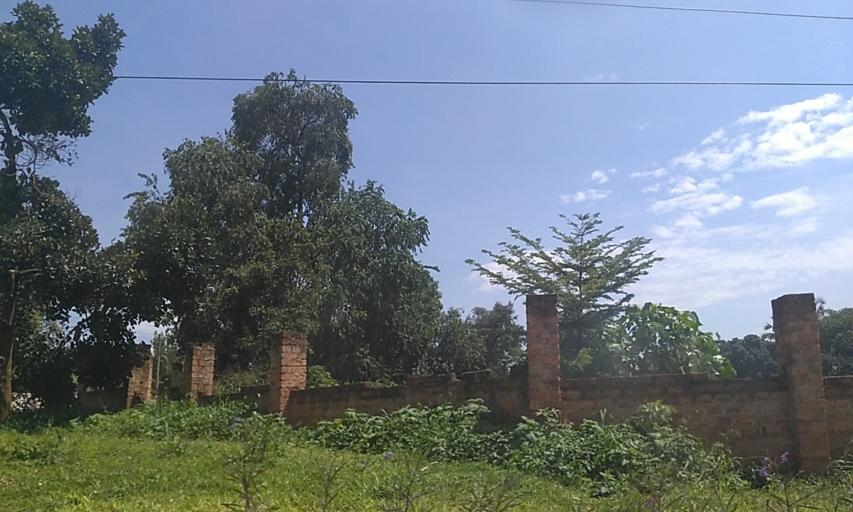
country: UG
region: Central Region
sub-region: Kampala District
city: Kampala
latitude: 0.3257
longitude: 32.6005
